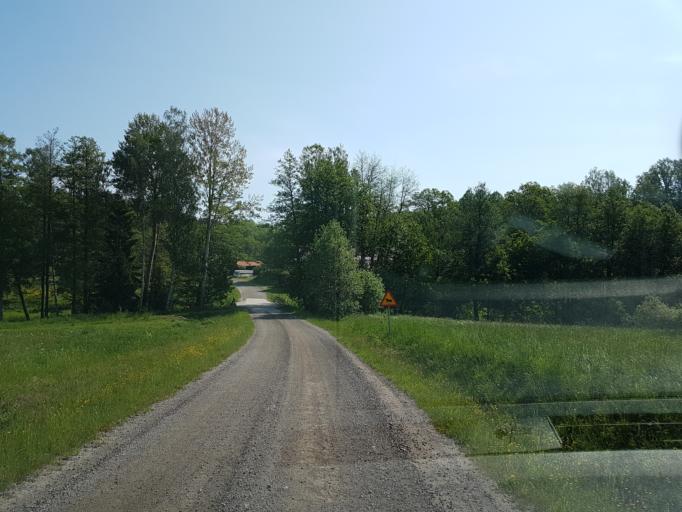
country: SE
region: OEstergoetland
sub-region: Atvidabergs Kommun
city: Atvidaberg
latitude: 58.1922
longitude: 16.1492
